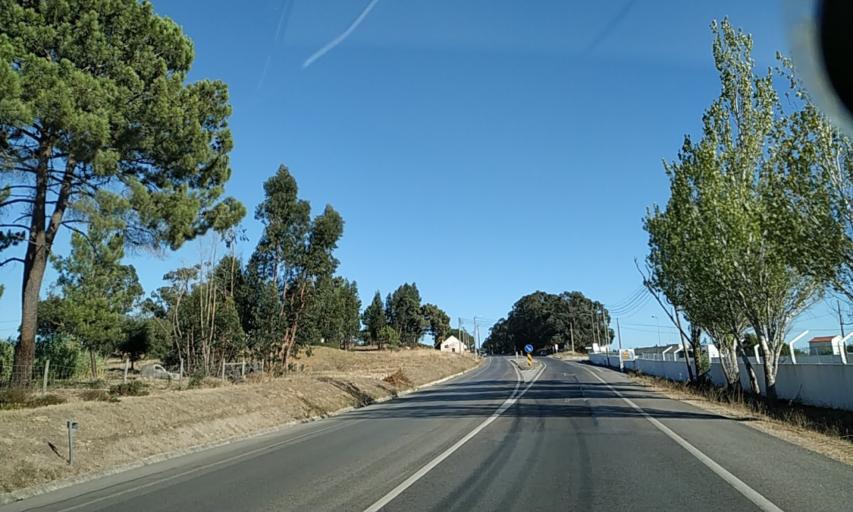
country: PT
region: Setubal
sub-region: Moita
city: Moita
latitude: 38.6334
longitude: -8.9700
